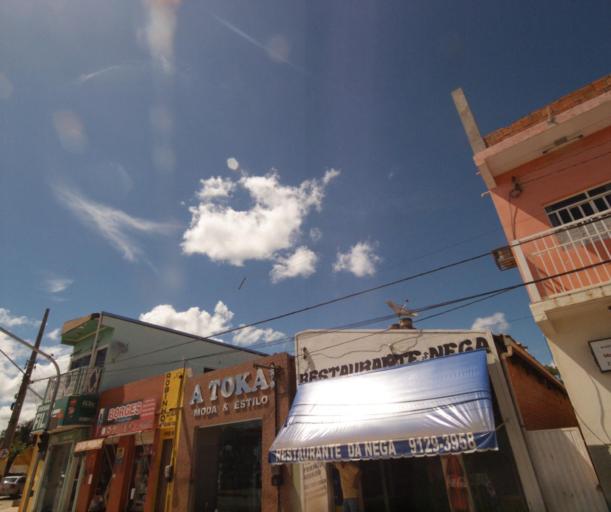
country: BR
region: Bahia
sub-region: Sao Felix Do Coribe
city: Santa Maria da Vitoria
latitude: -13.4040
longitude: -44.1941
